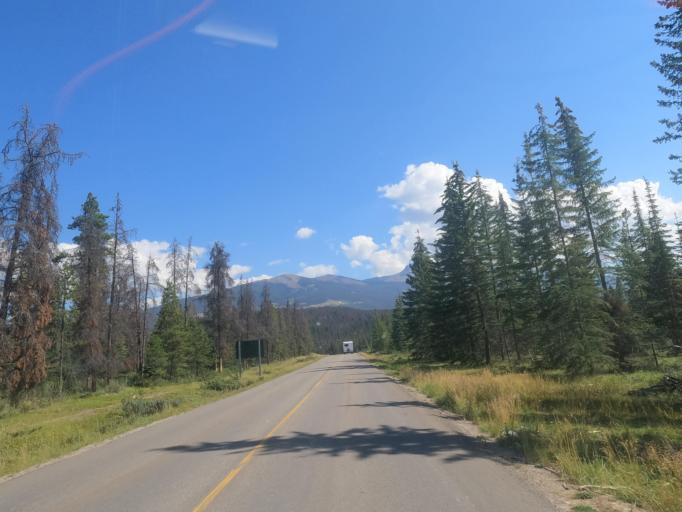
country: CA
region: Alberta
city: Jasper Park Lodge
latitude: 52.8540
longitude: -118.0852
